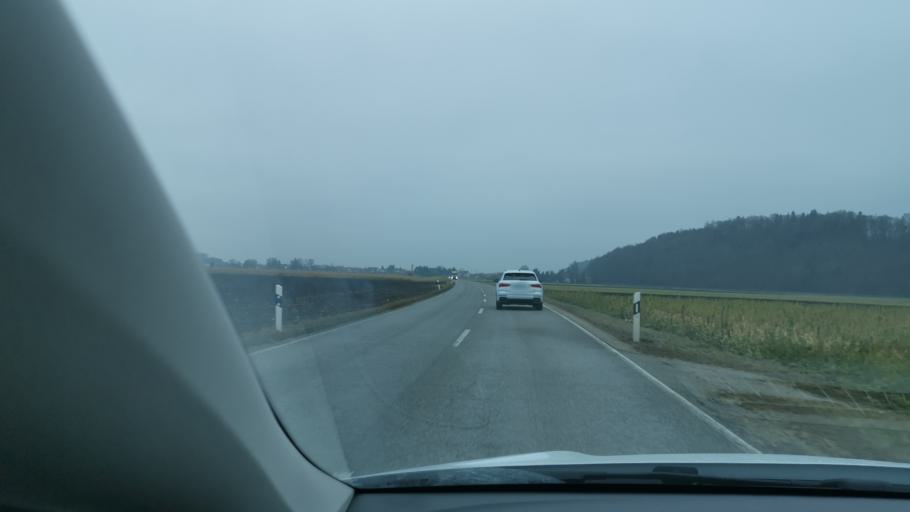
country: DE
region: Bavaria
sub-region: Swabia
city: Todtenweis
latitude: 48.5059
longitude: 10.9202
